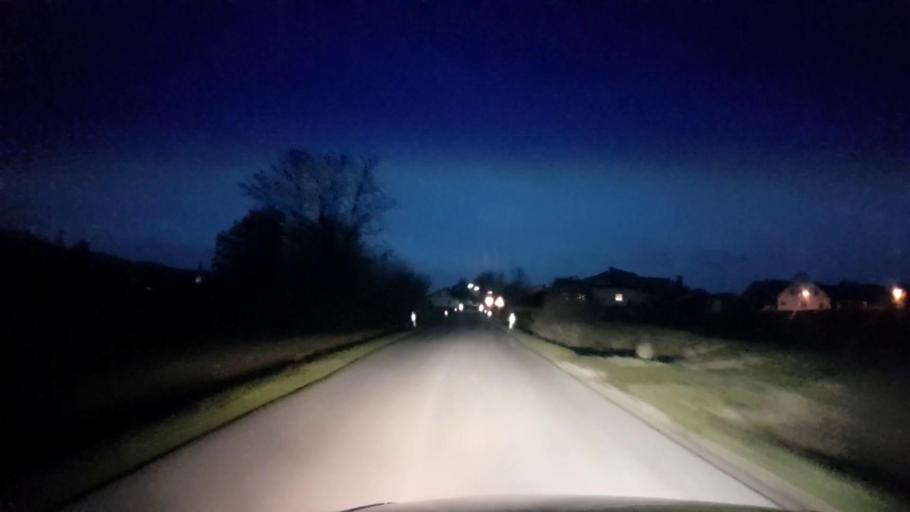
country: DE
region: Bavaria
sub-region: Upper Franconia
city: Burgebrach
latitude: 49.8465
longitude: 10.7391
